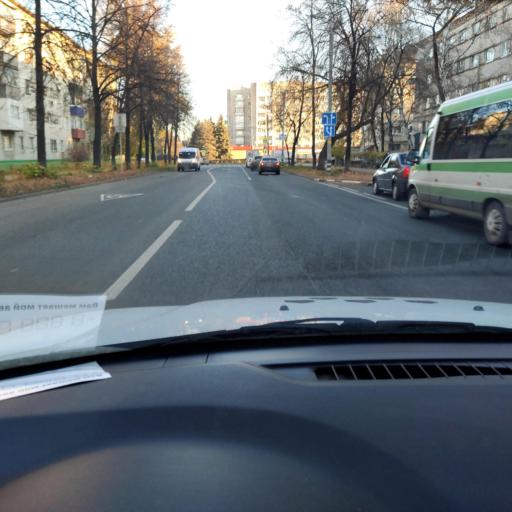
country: RU
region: Samara
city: Tol'yatti
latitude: 53.5199
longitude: 49.4264
